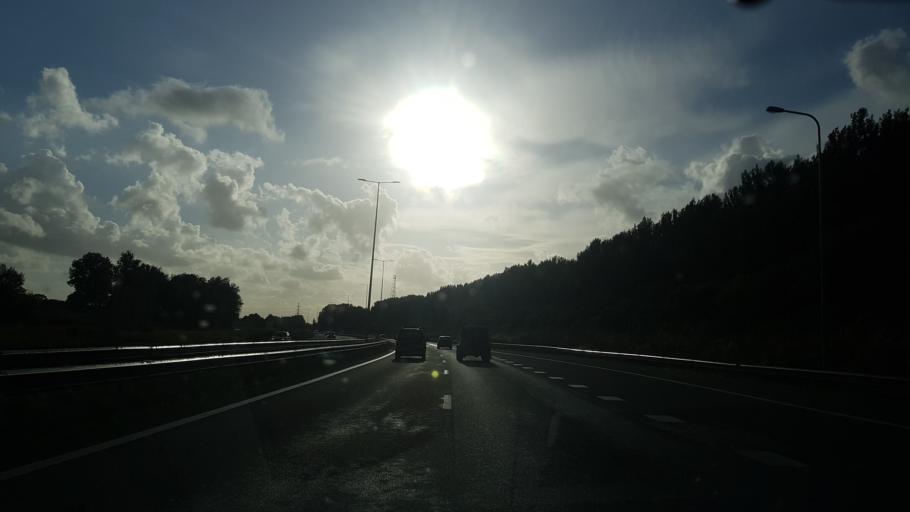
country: NL
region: Groningen
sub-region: Gemeente Zuidhorn
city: Aduard
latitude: 53.2030
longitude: 6.5008
